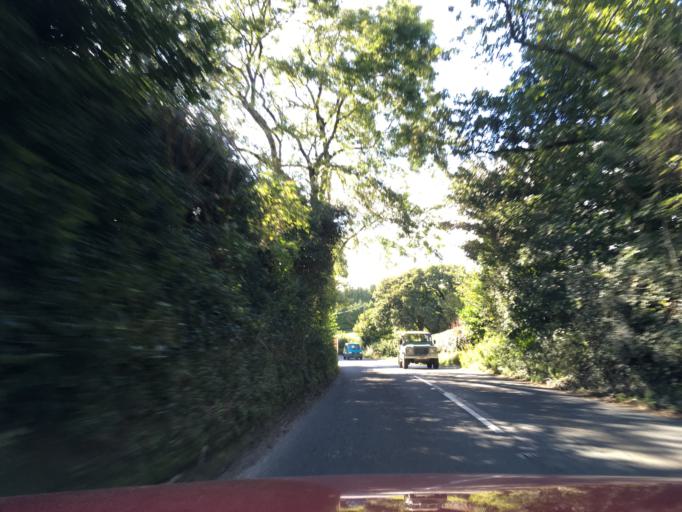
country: GB
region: England
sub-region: Devon
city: Buckfastleigh
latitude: 50.4310
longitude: -3.7701
